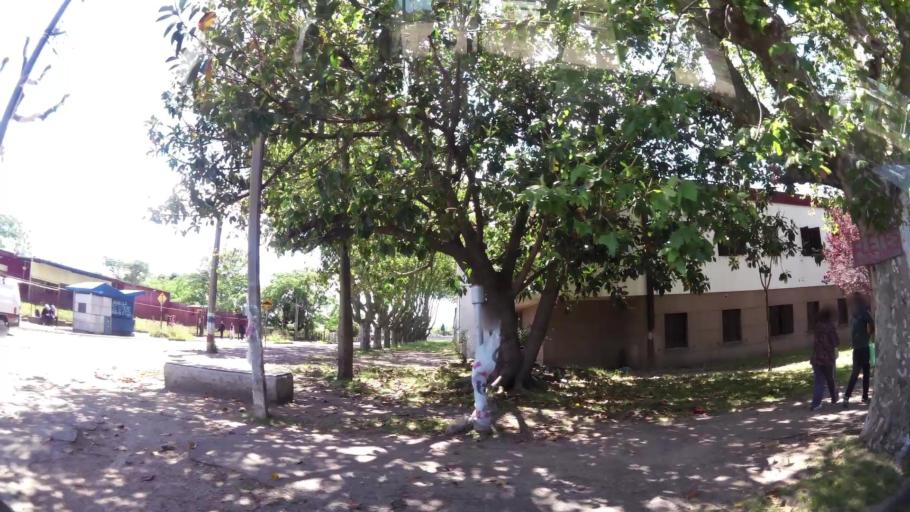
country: UY
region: Montevideo
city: Montevideo
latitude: -34.8327
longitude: -56.1403
